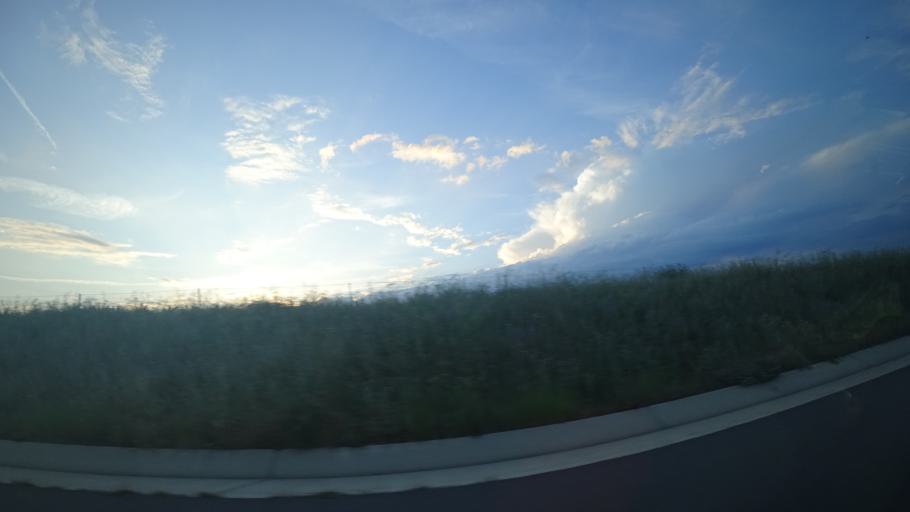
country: FR
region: Languedoc-Roussillon
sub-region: Departement de l'Herault
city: Servian
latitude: 43.3923
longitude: 3.3223
